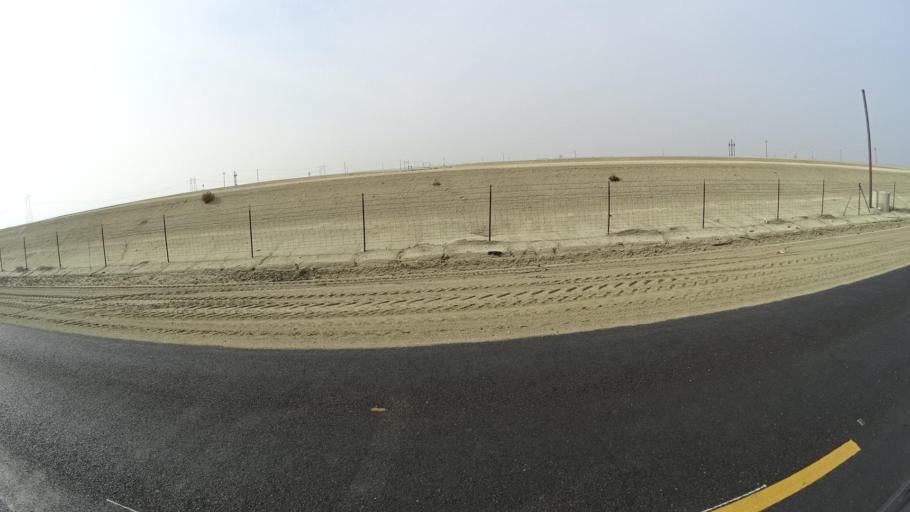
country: US
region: California
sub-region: Kern County
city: Arvin
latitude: 35.1262
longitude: -118.8506
